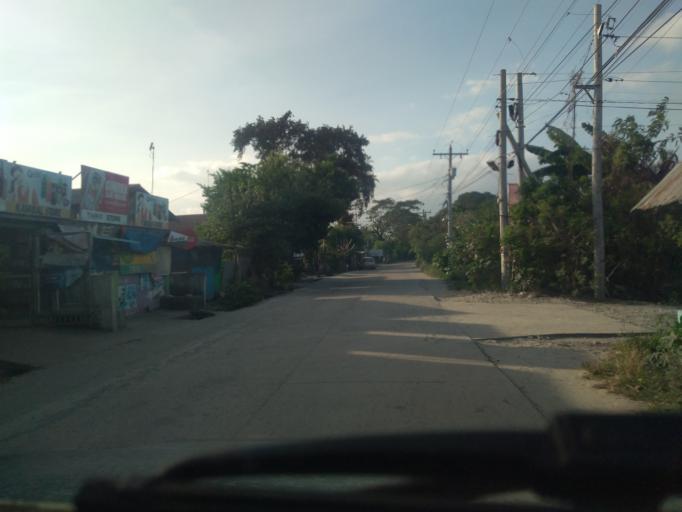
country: PH
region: Central Luzon
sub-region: Province of Pampanga
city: Malino
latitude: 15.1038
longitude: 120.6749
